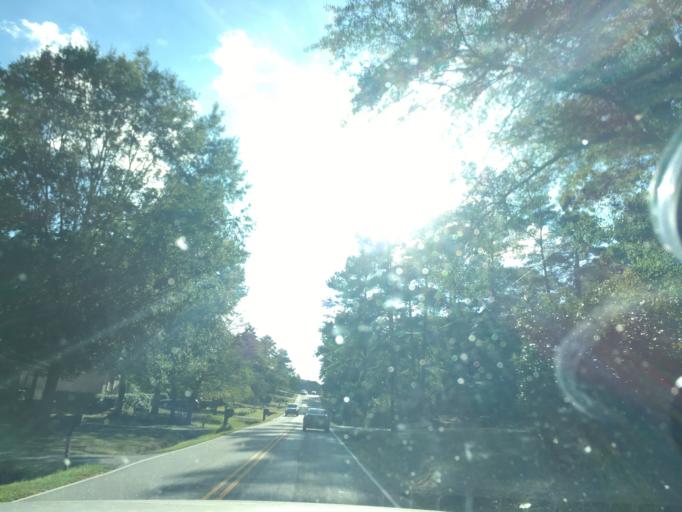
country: US
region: South Carolina
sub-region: Lexington County
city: Irmo
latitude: 34.0627
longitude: -81.1760
